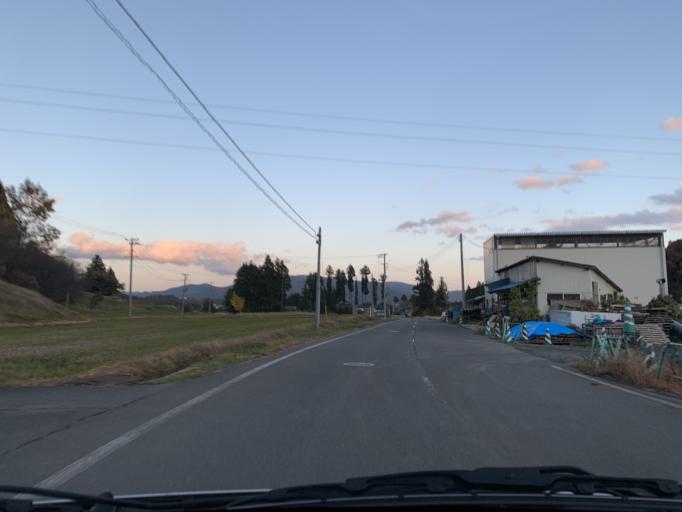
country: JP
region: Iwate
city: Ichinoseki
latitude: 39.0138
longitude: 141.0787
